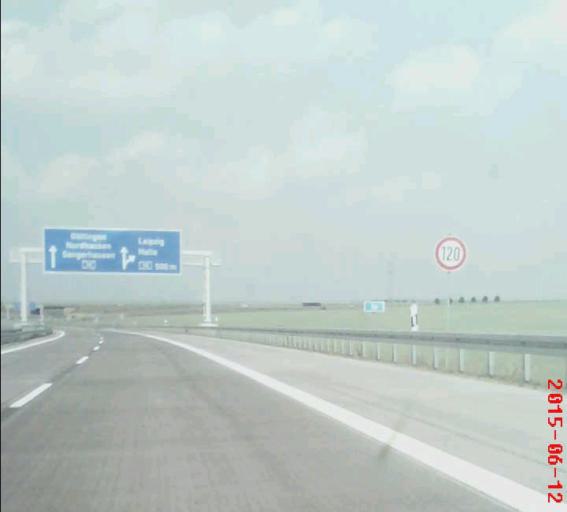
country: DE
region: Saxony-Anhalt
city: Oberroblingen
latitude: 51.4316
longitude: 11.3274
